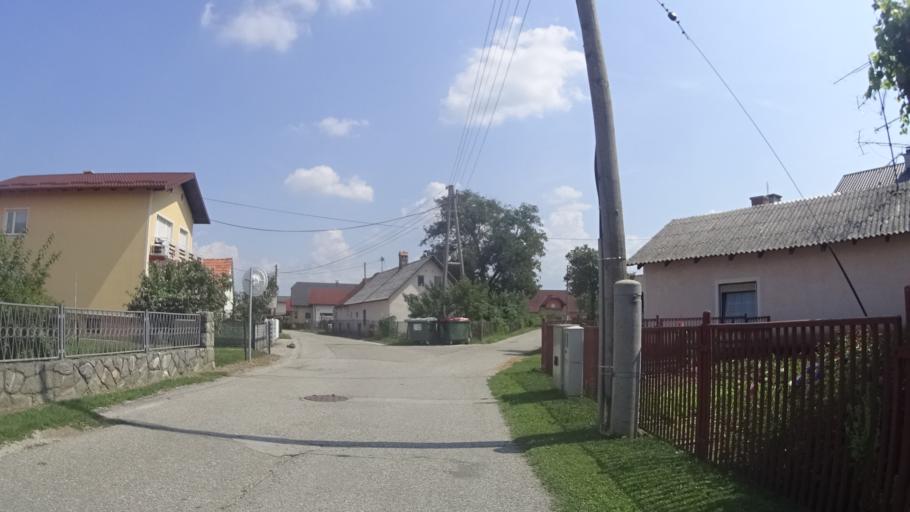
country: SI
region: Starse
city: Starse
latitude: 46.4504
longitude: 15.7382
